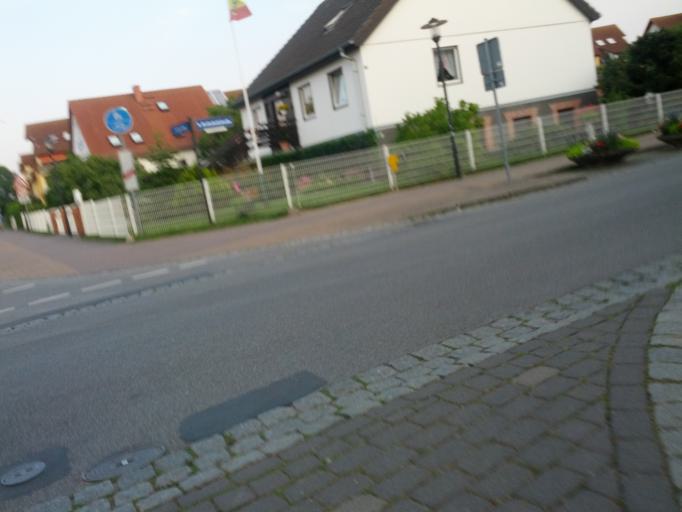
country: DE
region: Mecklenburg-Vorpommern
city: Ostseebad Kuhlungsborn
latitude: 54.1504
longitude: 11.7607
